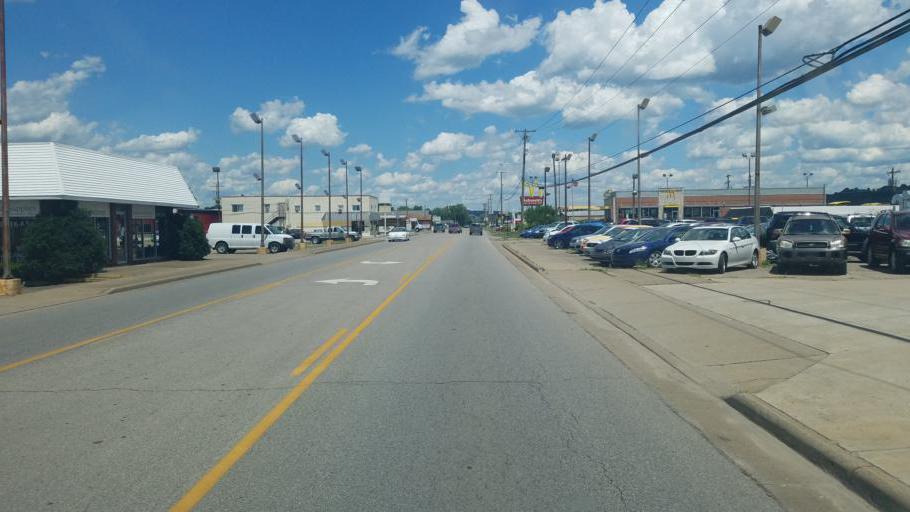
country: US
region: Ohio
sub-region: Gallia County
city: Gallipolis
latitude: 38.8197
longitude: -82.1802
